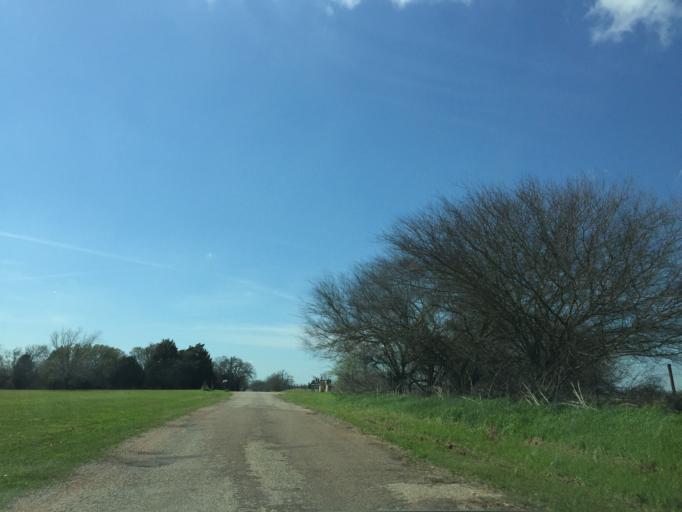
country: US
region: Texas
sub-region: Milam County
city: Thorndale
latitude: 30.5682
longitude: -97.1526
